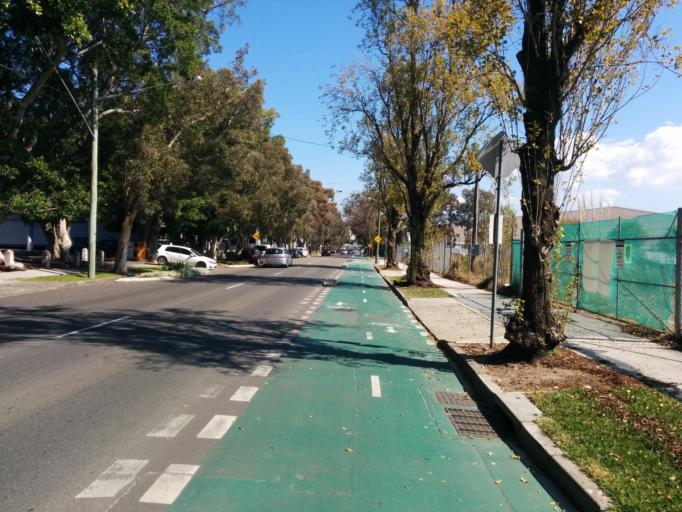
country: AU
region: New South Wales
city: Alexandria
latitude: -33.9149
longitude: 151.1913
